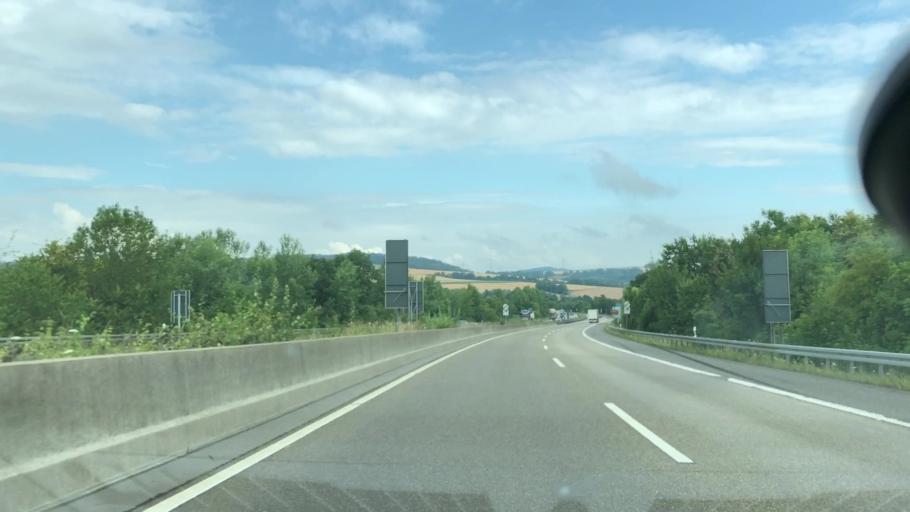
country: DE
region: Hesse
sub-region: Regierungsbezirk Kassel
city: Niederaula
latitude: 50.7680
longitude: 9.5892
